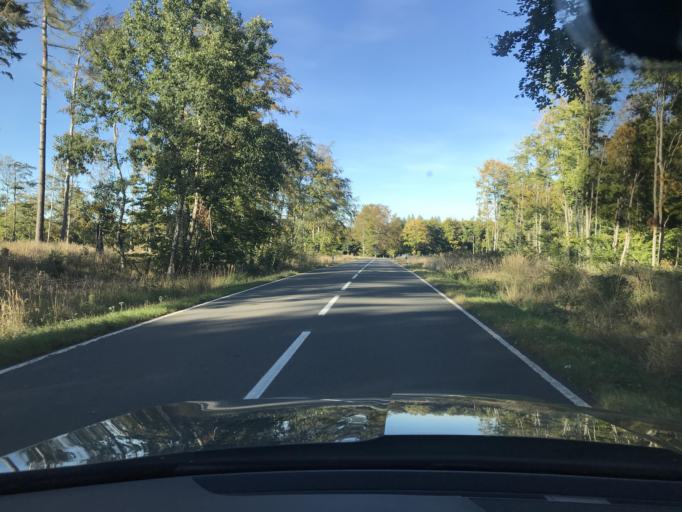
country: DE
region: Saxony-Anhalt
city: Friedrichsbrunn
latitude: 51.7188
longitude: 11.0148
